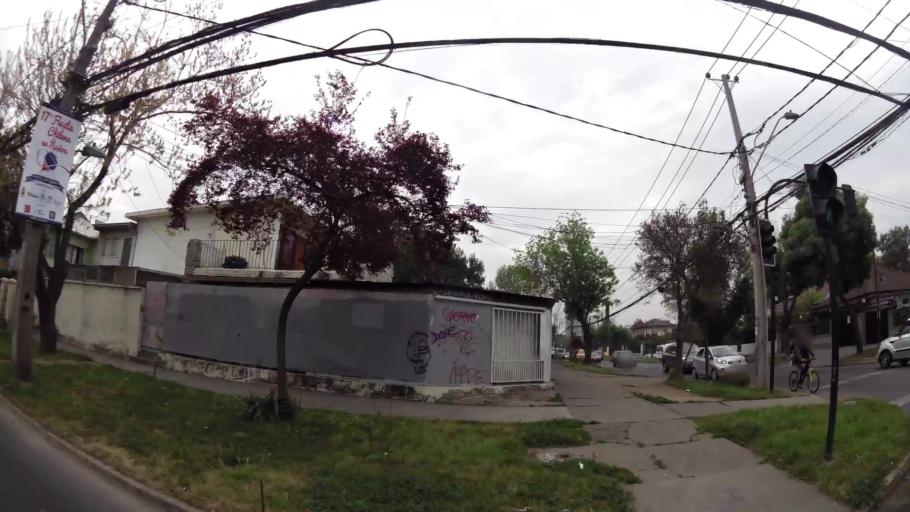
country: CL
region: Santiago Metropolitan
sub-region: Provincia de Santiago
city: Villa Presidente Frei, Nunoa, Santiago, Chile
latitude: -33.4600
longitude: -70.5847
